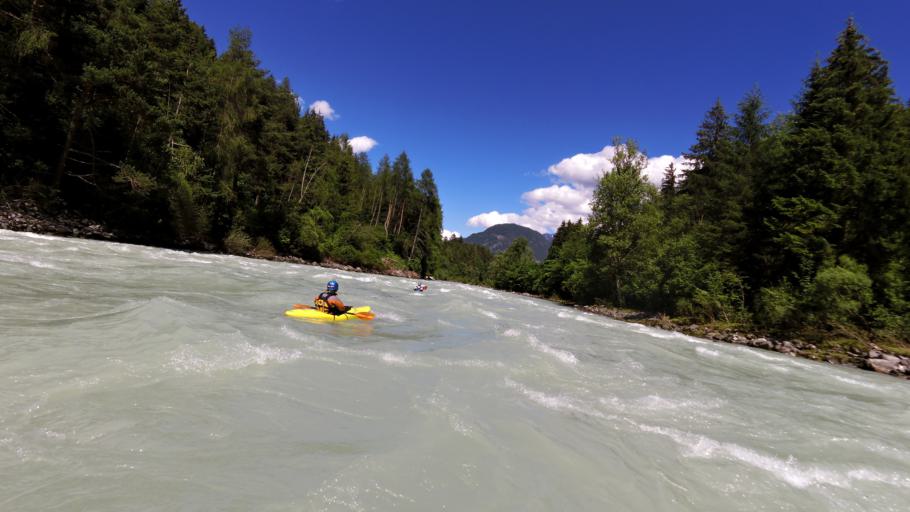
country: AT
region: Tyrol
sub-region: Politischer Bezirk Imst
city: Karres
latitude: 47.2114
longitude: 10.7998
